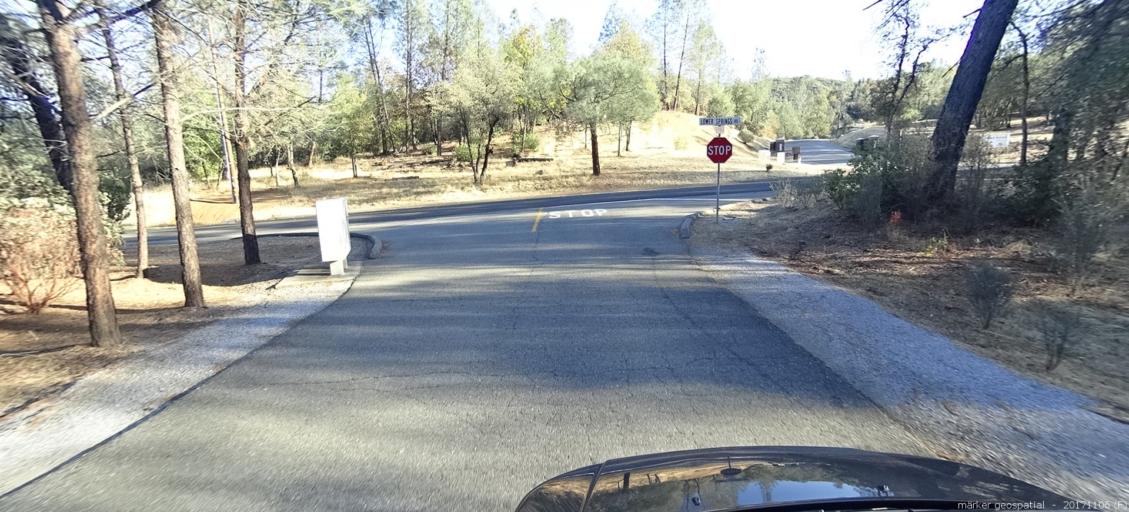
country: US
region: California
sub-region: Shasta County
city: Shasta
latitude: 40.5748
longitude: -122.4608
